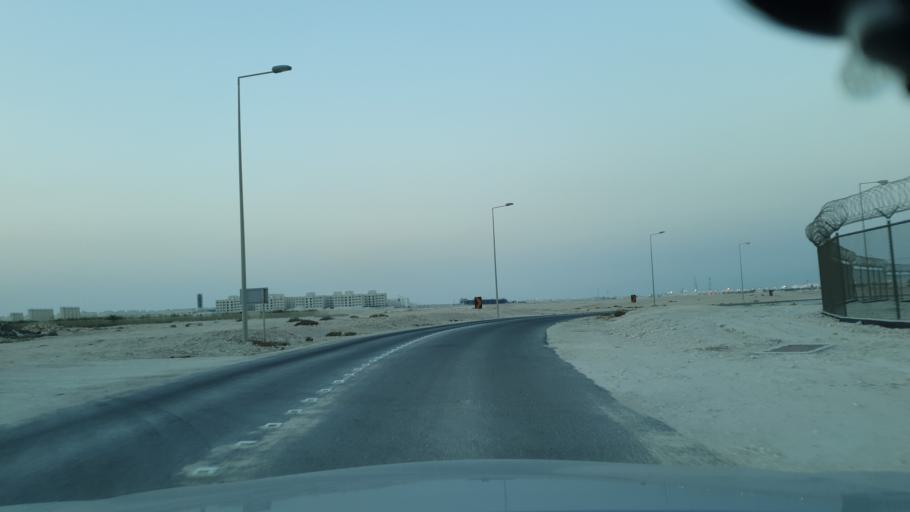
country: BH
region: Central Governorate
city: Dar Kulayb
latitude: 25.9755
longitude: 50.6095
